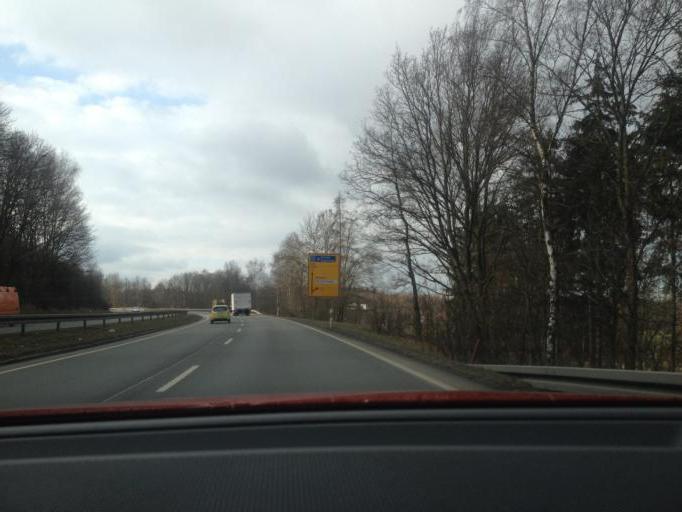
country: DE
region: Bavaria
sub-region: Upper Franconia
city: Hof
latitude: 50.2964
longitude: 11.9146
